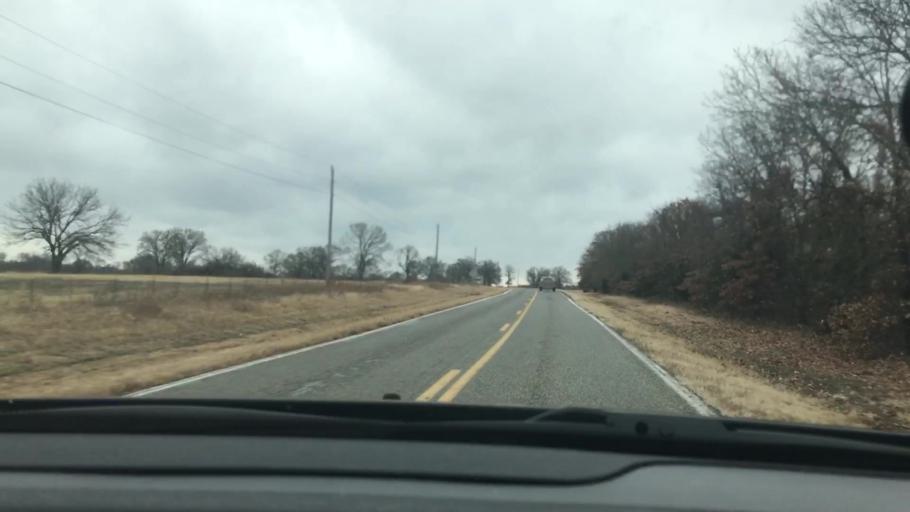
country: US
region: Oklahoma
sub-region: Johnston County
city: Tishomingo
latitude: 34.1889
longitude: -96.5793
